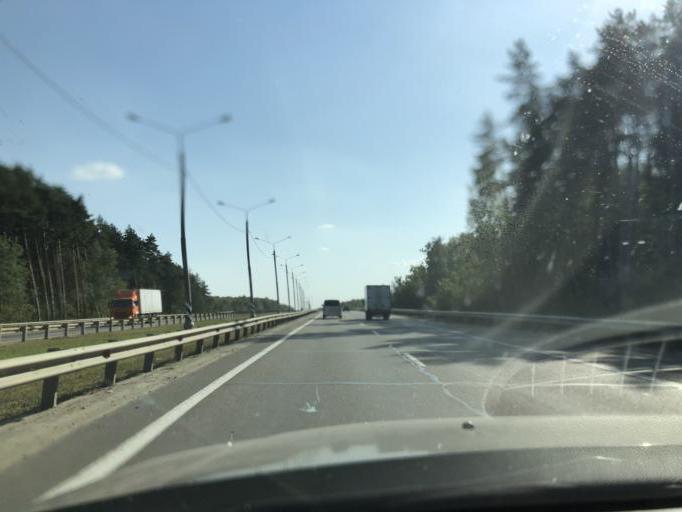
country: RU
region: Tula
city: Zaokskiy
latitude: 54.6723
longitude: 37.5040
